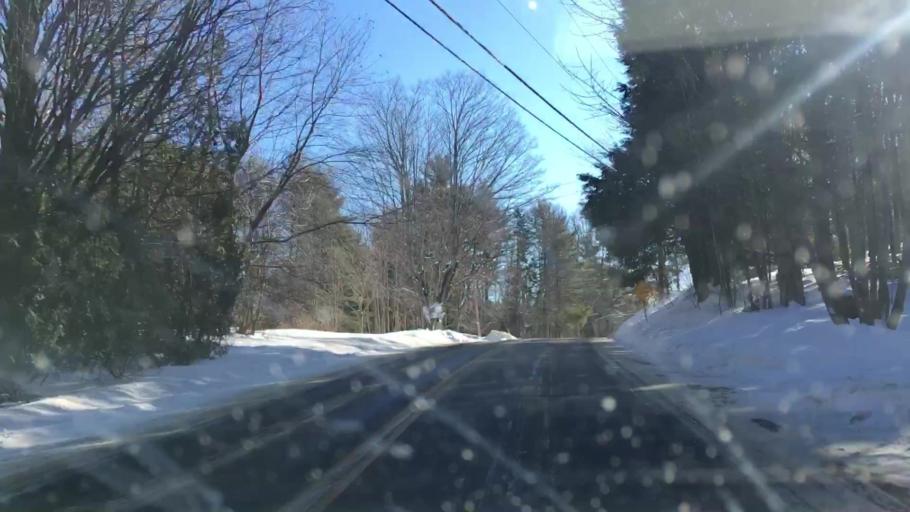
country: US
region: Maine
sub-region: Sagadahoc County
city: Topsham
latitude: 43.9126
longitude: -70.0187
